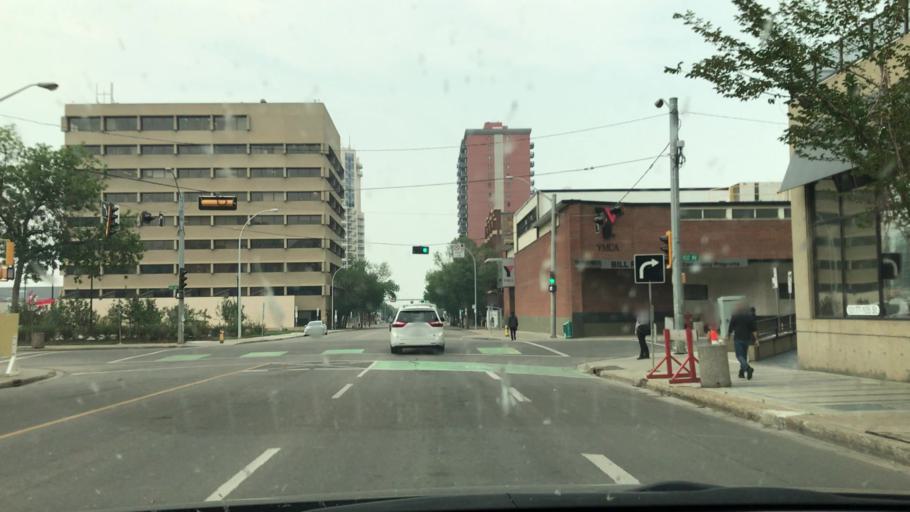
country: CA
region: Alberta
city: Edmonton
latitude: 53.5426
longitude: -113.5011
